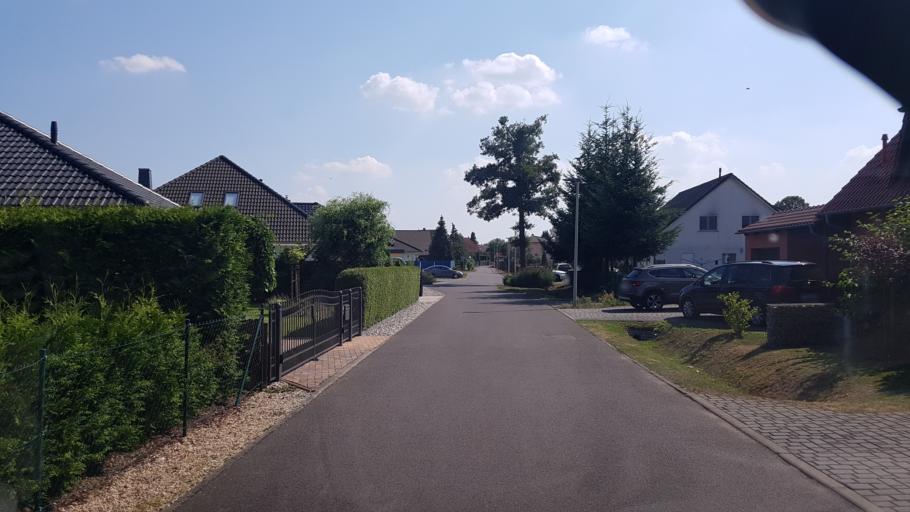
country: DE
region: Brandenburg
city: Cottbus
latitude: 51.7187
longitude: 14.4179
